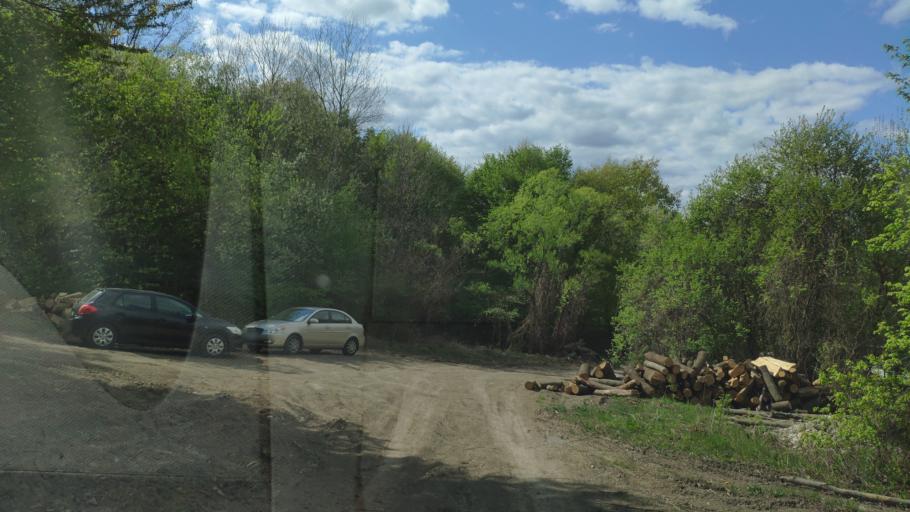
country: SK
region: Kosicky
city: Kosice
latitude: 48.6762
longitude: 21.4457
